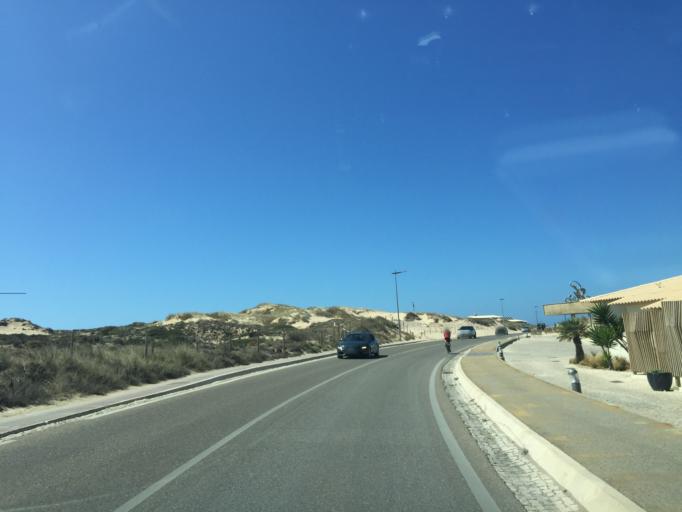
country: PT
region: Lisbon
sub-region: Cascais
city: Cascais
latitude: 38.7246
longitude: -9.4748
